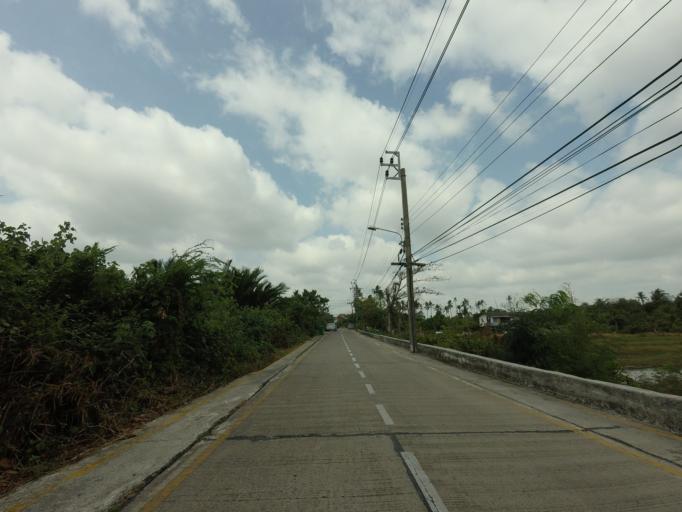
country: TH
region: Samut Prakan
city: Phra Pradaeng
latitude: 13.6609
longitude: 100.5605
